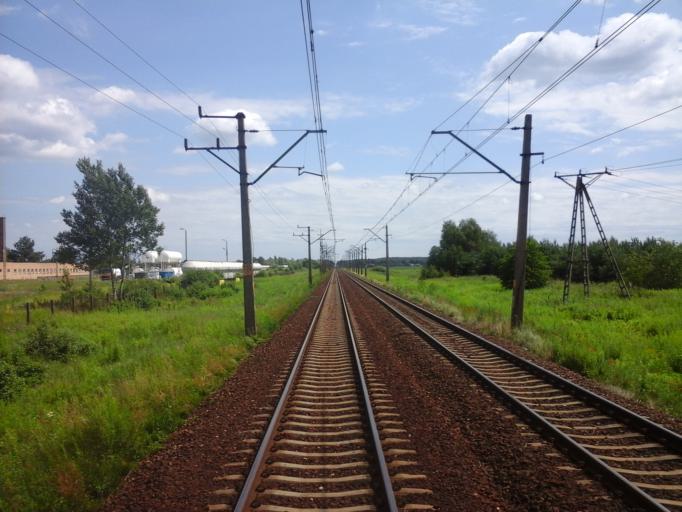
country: PL
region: West Pomeranian Voivodeship
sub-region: Powiat gryfinski
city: Stare Czarnowo
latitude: 53.3880
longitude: 14.7189
